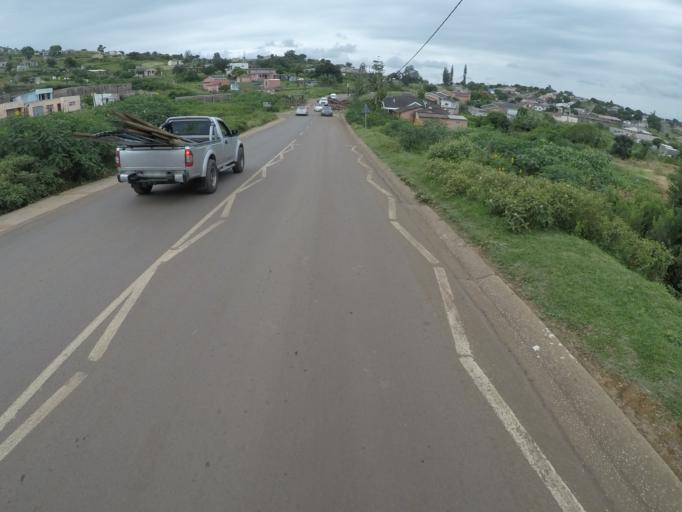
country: ZA
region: KwaZulu-Natal
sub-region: uThungulu District Municipality
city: Empangeni
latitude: -28.7730
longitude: 31.8499
